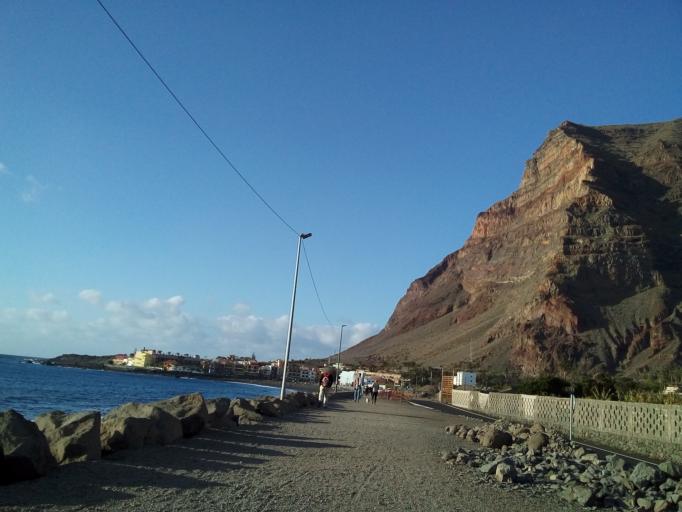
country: ES
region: Canary Islands
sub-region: Provincia de Santa Cruz de Tenerife
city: Alajero
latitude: 28.0906
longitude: -17.3397
